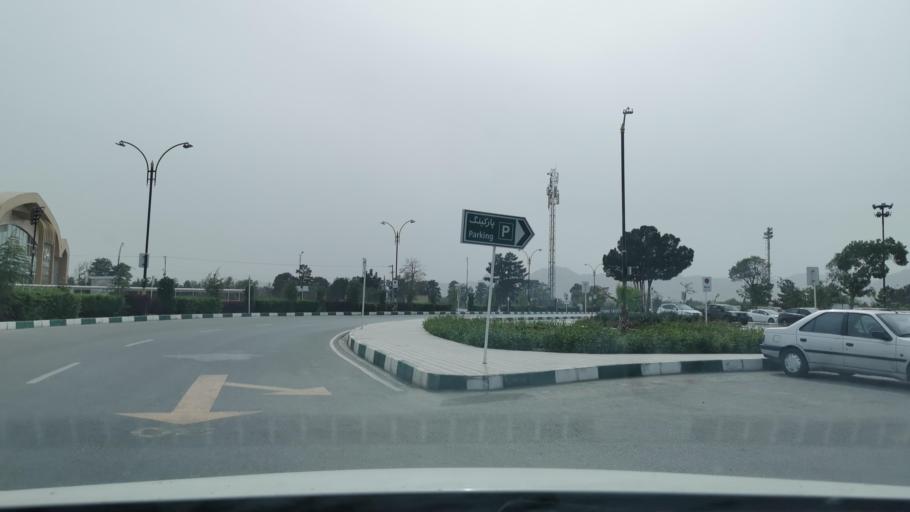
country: IR
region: Razavi Khorasan
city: Mashhad
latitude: 36.2259
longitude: 59.6421
